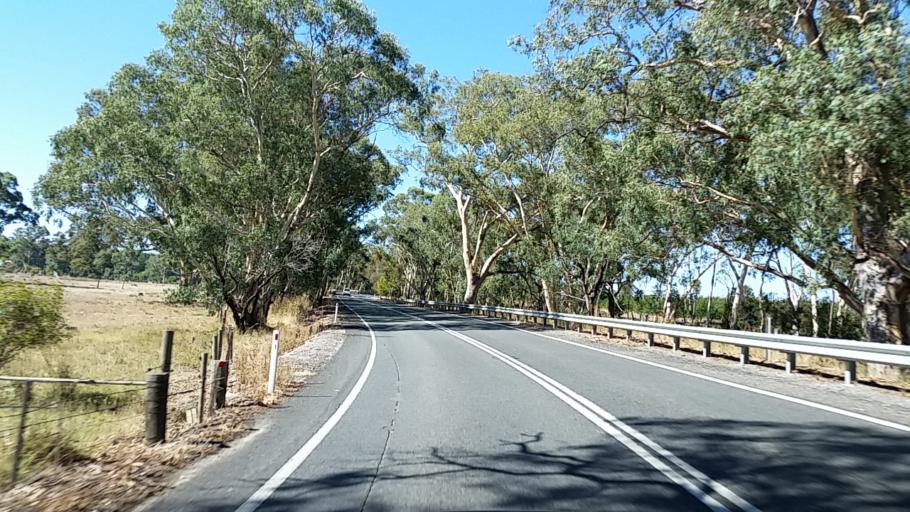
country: AU
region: South Australia
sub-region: Adelaide Hills
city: Birdwood
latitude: -34.7351
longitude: 138.9658
